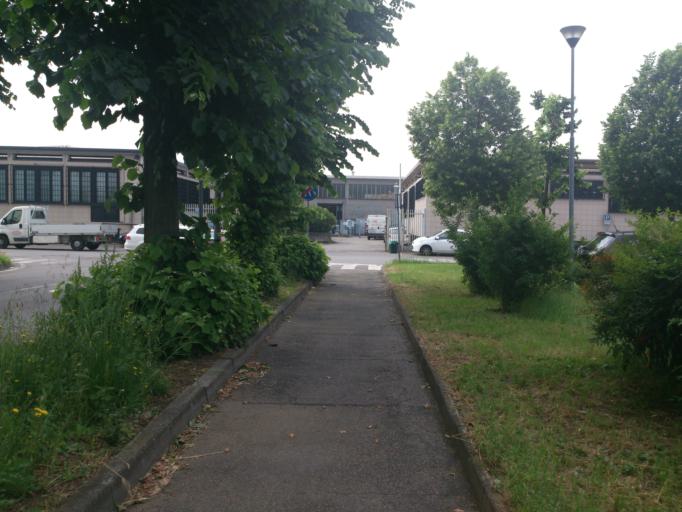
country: IT
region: Lombardy
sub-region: Provincia di Monza e Brianza
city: Agrate Brianza
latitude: 45.5676
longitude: 9.3337
